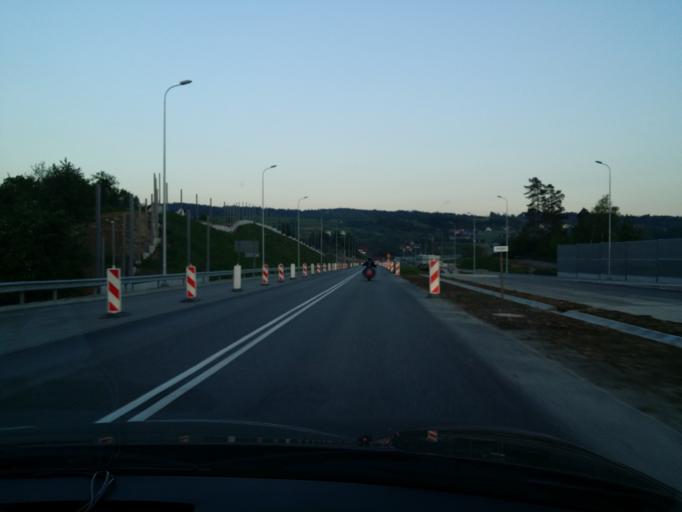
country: PL
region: Lesser Poland Voivodeship
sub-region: Powiat nowotarski
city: Rokiciny
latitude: 49.6021
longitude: 19.9267
